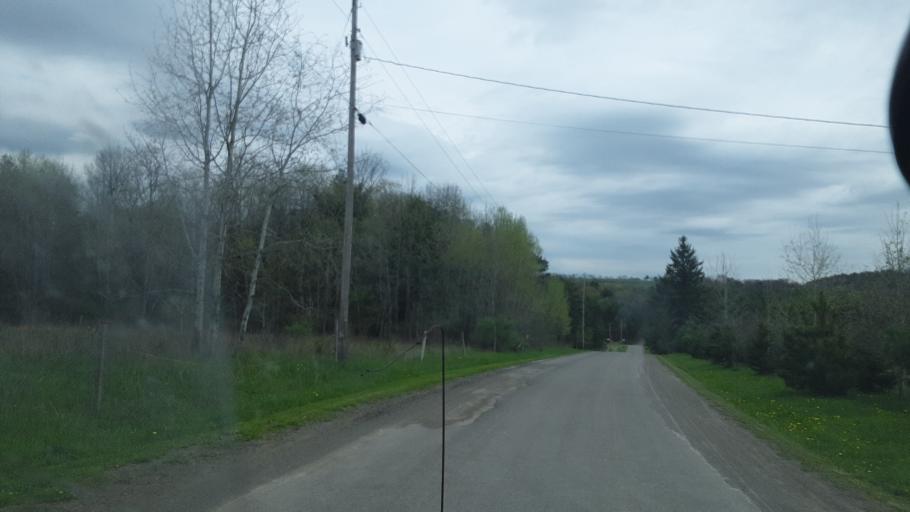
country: US
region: New York
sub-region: Steuben County
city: Addison
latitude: 42.0930
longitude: -77.3081
